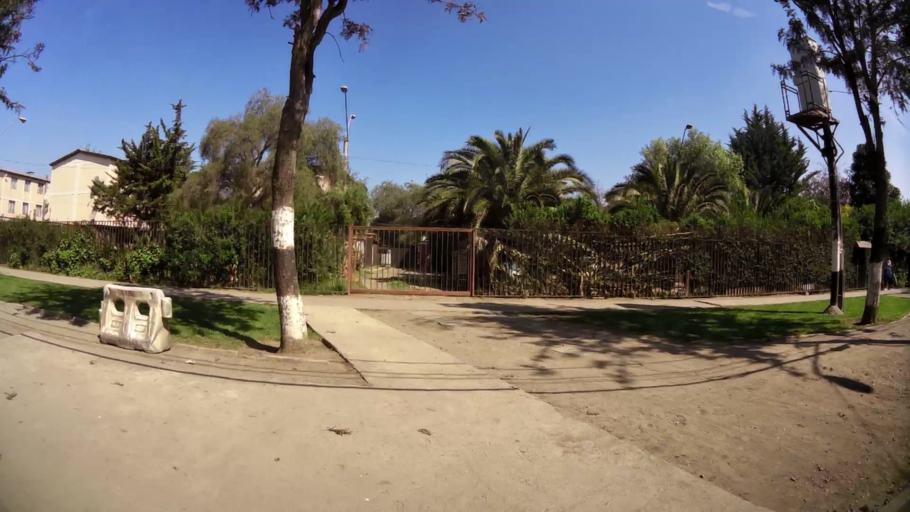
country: CL
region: Santiago Metropolitan
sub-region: Provincia de Santiago
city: Lo Prado
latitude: -33.5061
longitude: -70.7869
